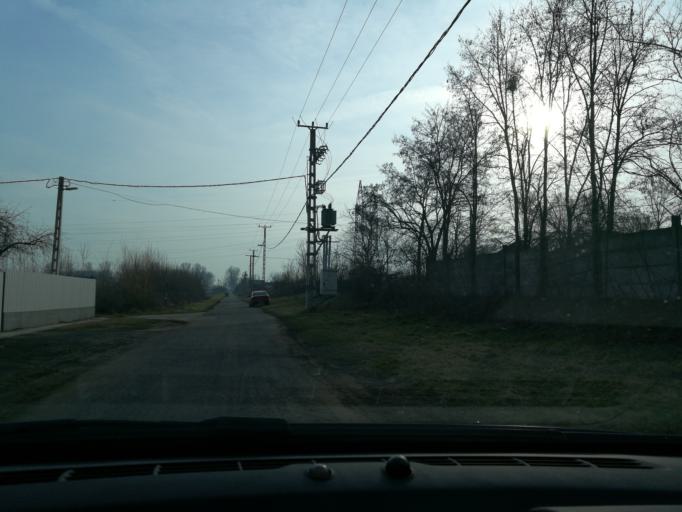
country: HU
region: Szabolcs-Szatmar-Bereg
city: Nyiregyhaza
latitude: 47.9374
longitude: 21.7004
